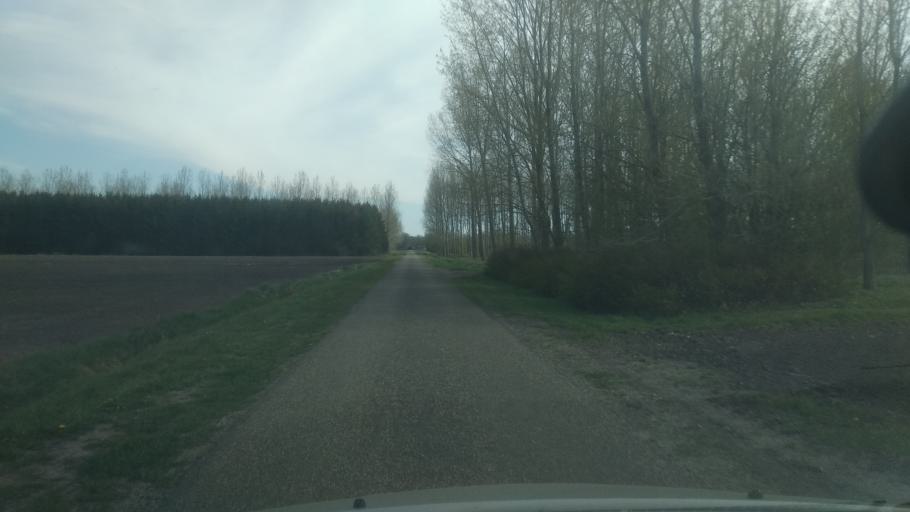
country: NL
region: Drenthe
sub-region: Gemeente Borger-Odoorn
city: Borger
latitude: 52.9636
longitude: 6.8669
